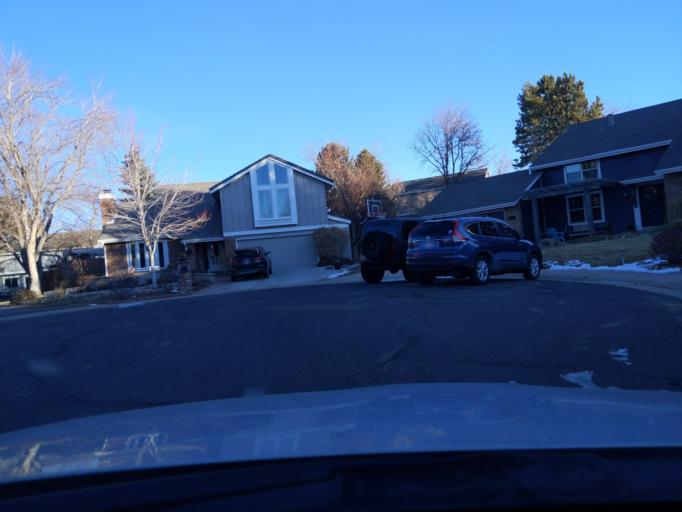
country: US
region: Colorado
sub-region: Arapahoe County
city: Centennial
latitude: 39.5720
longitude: -104.8885
